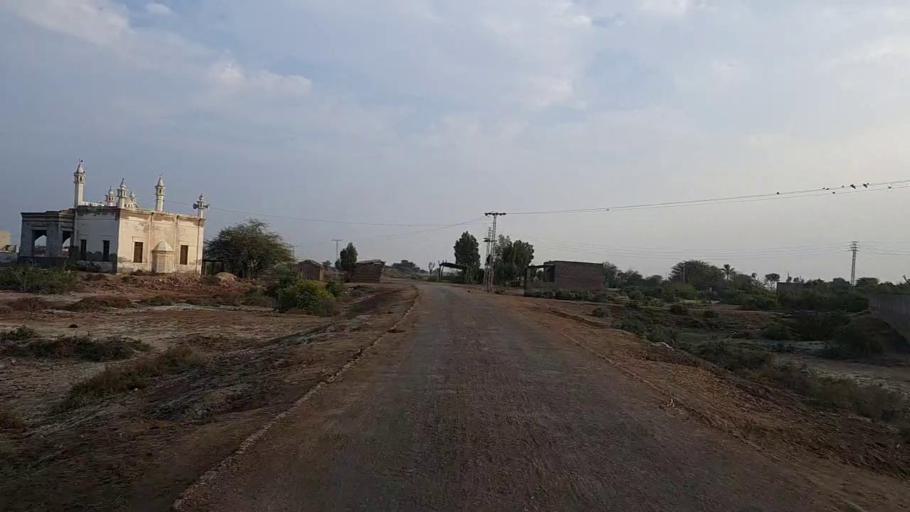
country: PK
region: Sindh
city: Pithoro
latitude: 25.4502
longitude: 69.2878
